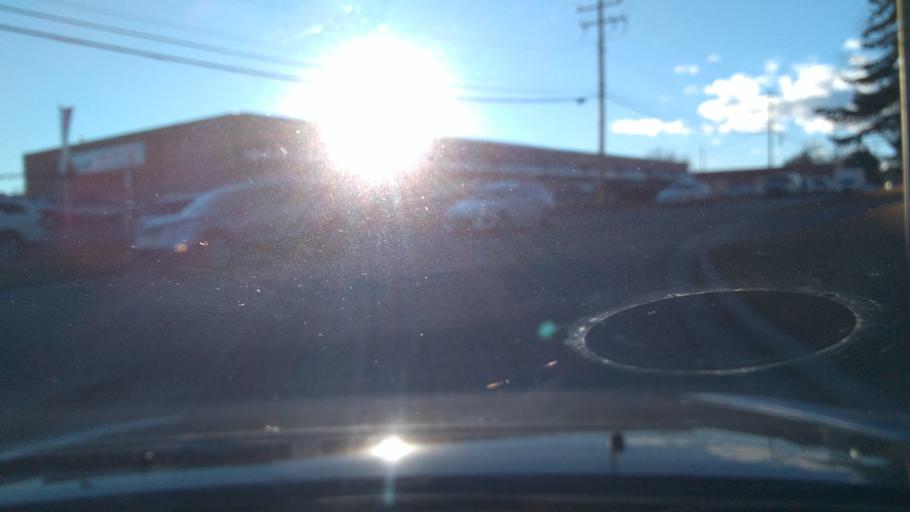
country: CA
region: Alberta
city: Calgary
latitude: 50.9846
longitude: -114.0489
